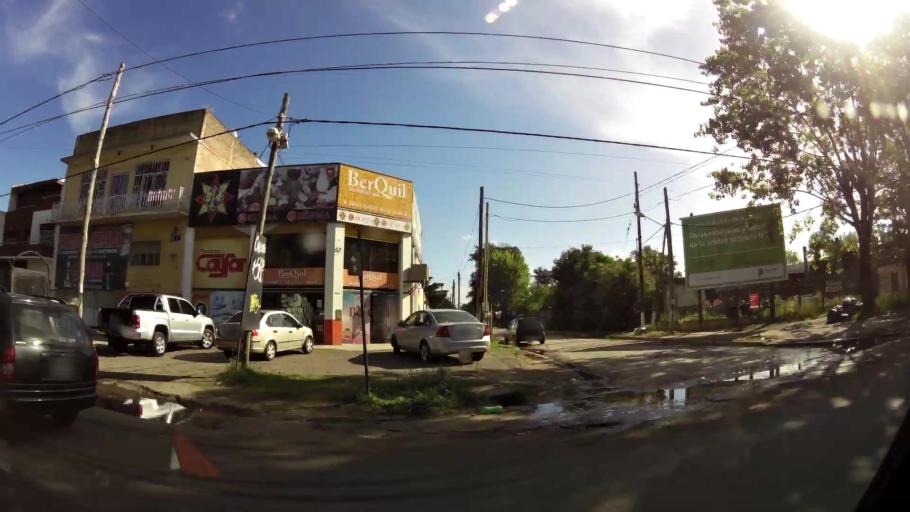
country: AR
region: Buenos Aires
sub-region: Partido de Quilmes
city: Quilmes
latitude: -34.7982
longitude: -58.2303
